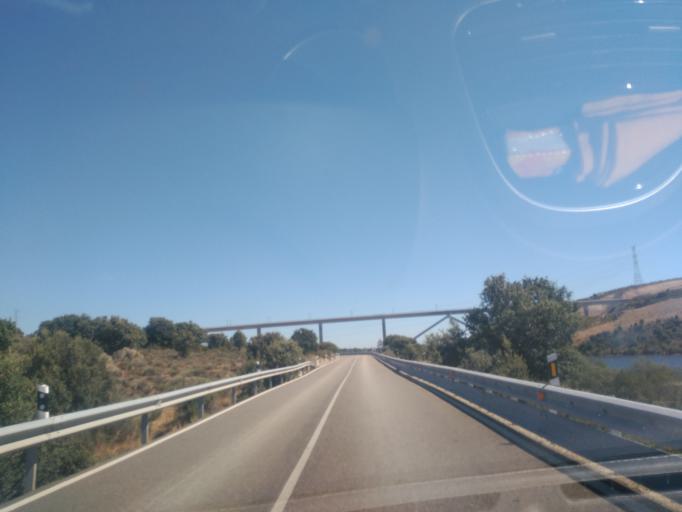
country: ES
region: Castille and Leon
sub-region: Provincia de Zamora
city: Villardeciervos
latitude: 41.9788
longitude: -6.2318
